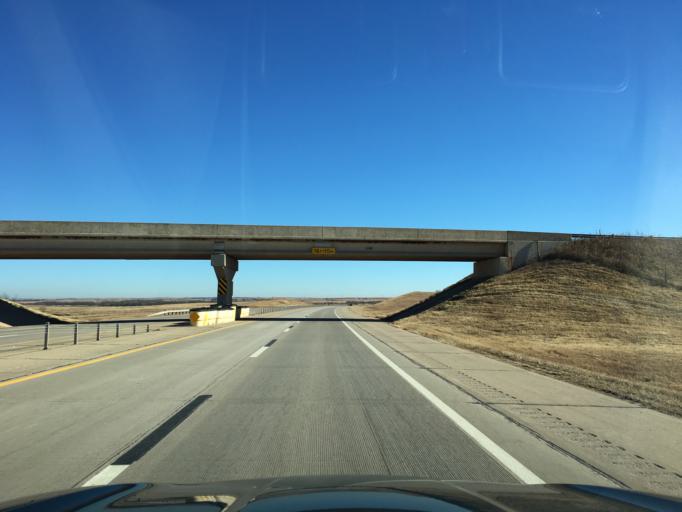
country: US
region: Oklahoma
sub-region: Noble County
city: Perry
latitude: 36.3916
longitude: -97.1044
